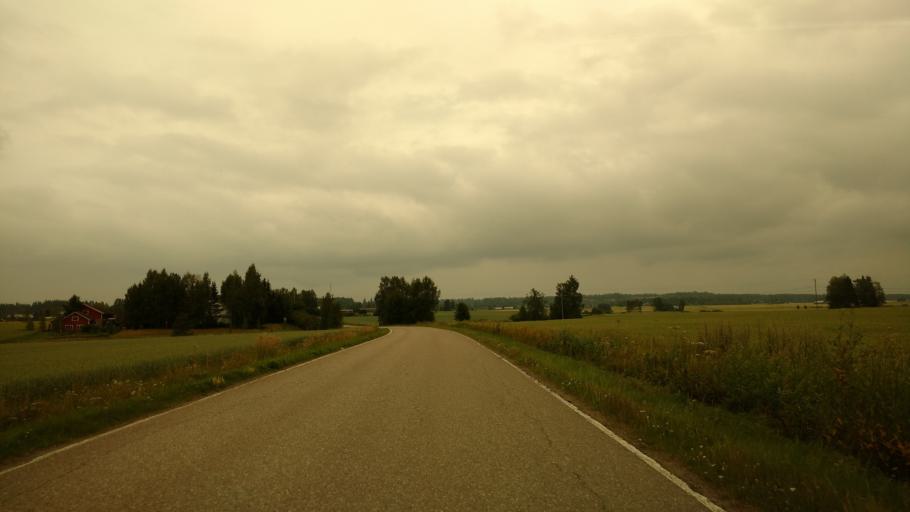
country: FI
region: Haeme
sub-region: Forssa
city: Ypaejae
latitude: 60.7823
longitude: 23.2695
